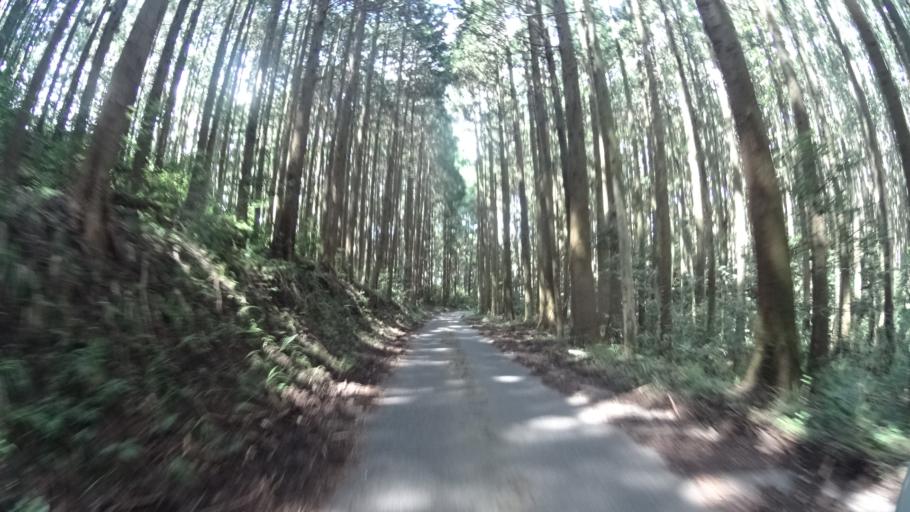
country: JP
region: Yamaguchi
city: Hagi
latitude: 34.4931
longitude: 131.5634
